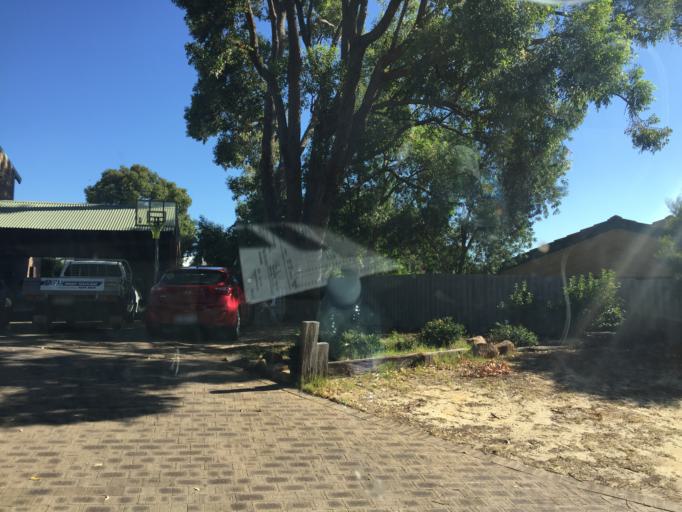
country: AU
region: Western Australia
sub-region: Mundaring
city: Swan View
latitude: -31.8812
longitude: 116.0405
